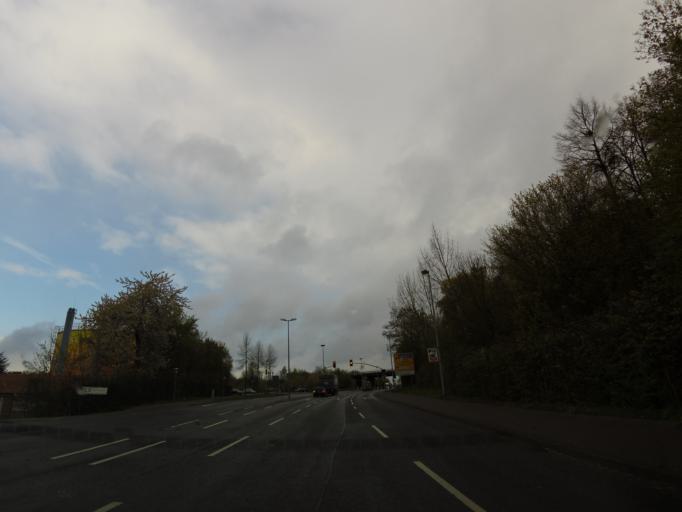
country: DE
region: Lower Saxony
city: Goettingen
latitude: 51.5543
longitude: 9.9199
